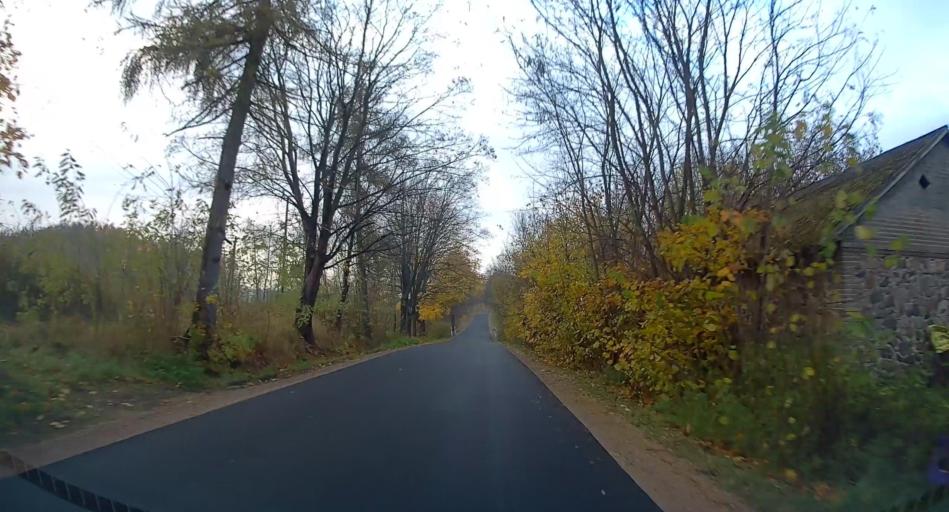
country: PL
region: Masovian Voivodeship
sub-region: Powiat zyrardowski
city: Puszcza Marianska
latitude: 51.9494
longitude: 20.3721
